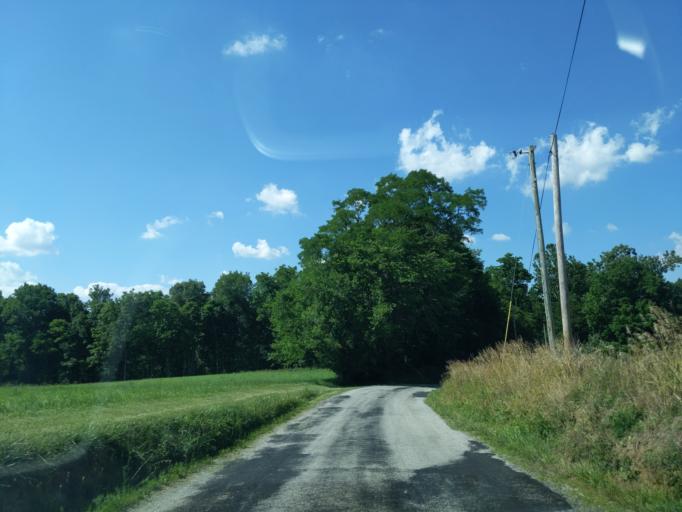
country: US
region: Indiana
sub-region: Ripley County
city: Osgood
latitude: 39.1908
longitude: -85.4213
